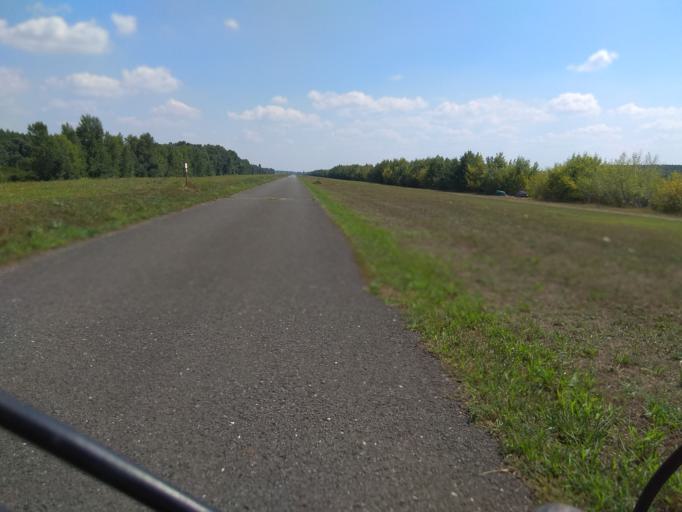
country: SK
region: Trnavsky
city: Gabcikovo
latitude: 47.8535
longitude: 17.5735
